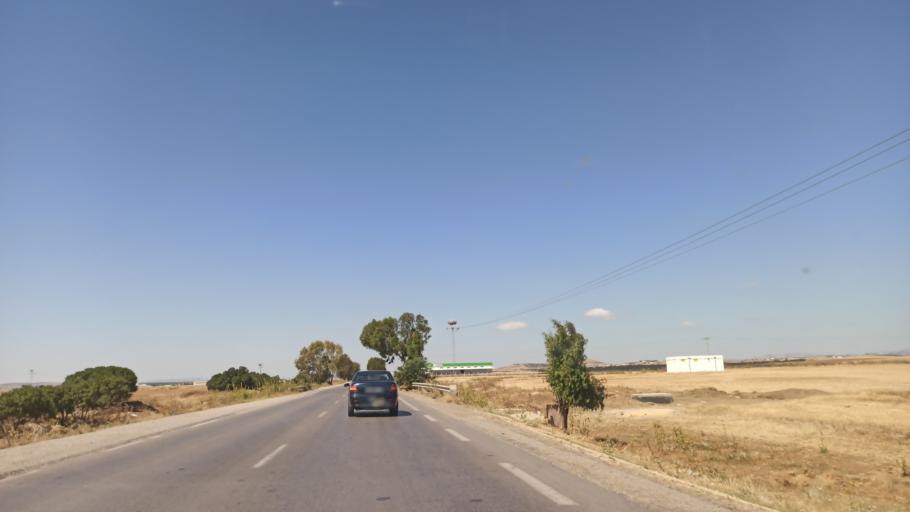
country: TN
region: Tunis
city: Oued Lill
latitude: 36.7419
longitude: 9.9569
